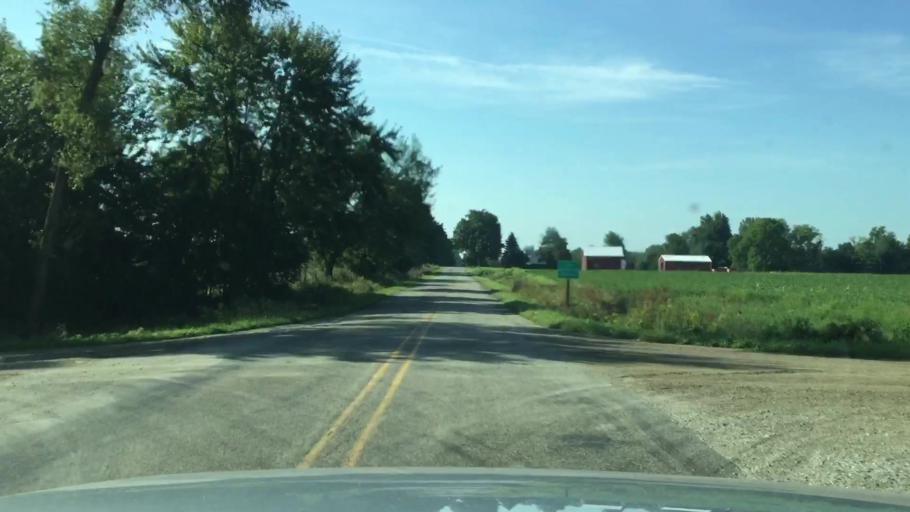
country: US
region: Michigan
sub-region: Lenawee County
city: Hudson
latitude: 41.8987
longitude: -84.4204
